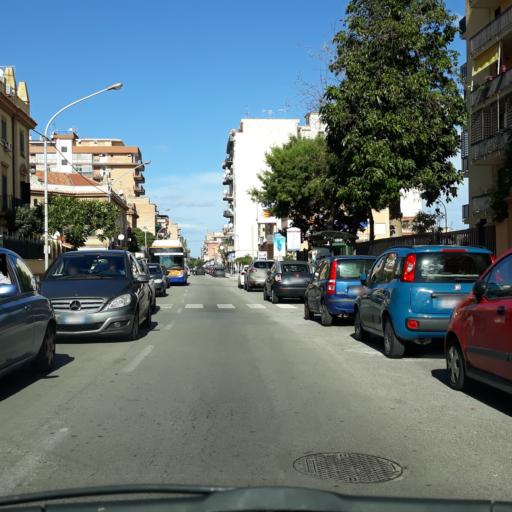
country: IT
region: Sicily
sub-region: Palermo
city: Palermo
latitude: 38.1484
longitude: 13.3708
